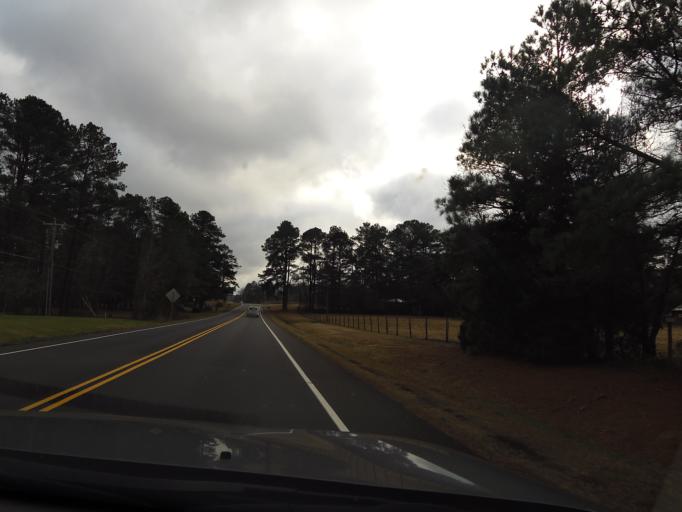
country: US
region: North Carolina
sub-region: Nash County
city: Rocky Mount
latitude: 35.8907
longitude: -77.7409
